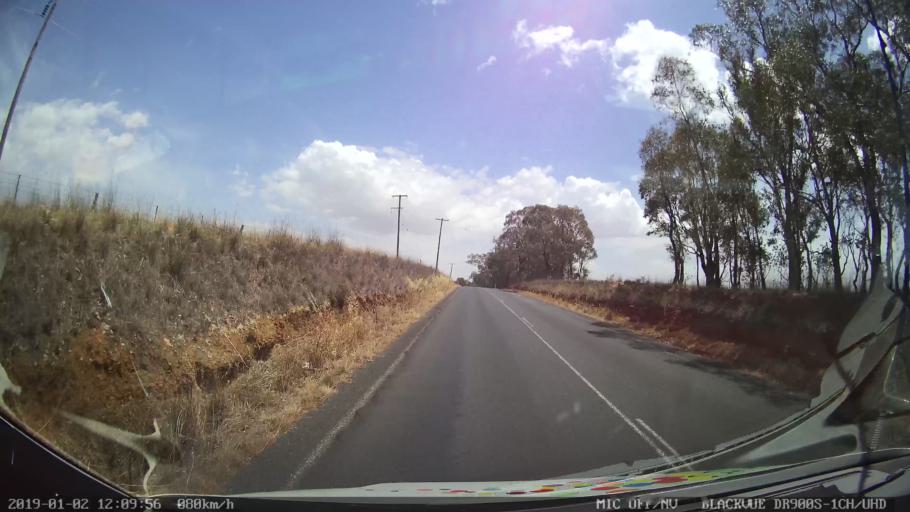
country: AU
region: New South Wales
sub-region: Young
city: Young
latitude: -34.4662
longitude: 148.2669
